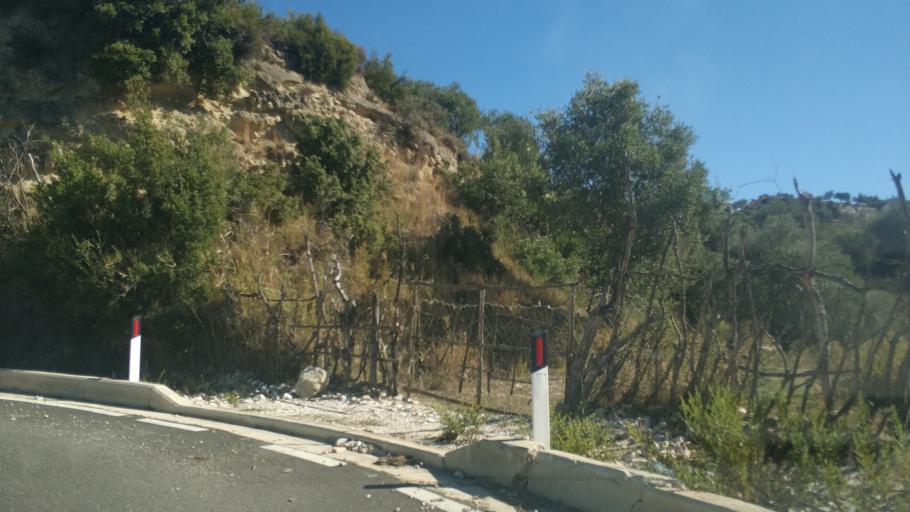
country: AL
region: Vlore
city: Vlore
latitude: 40.4568
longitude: 19.5108
